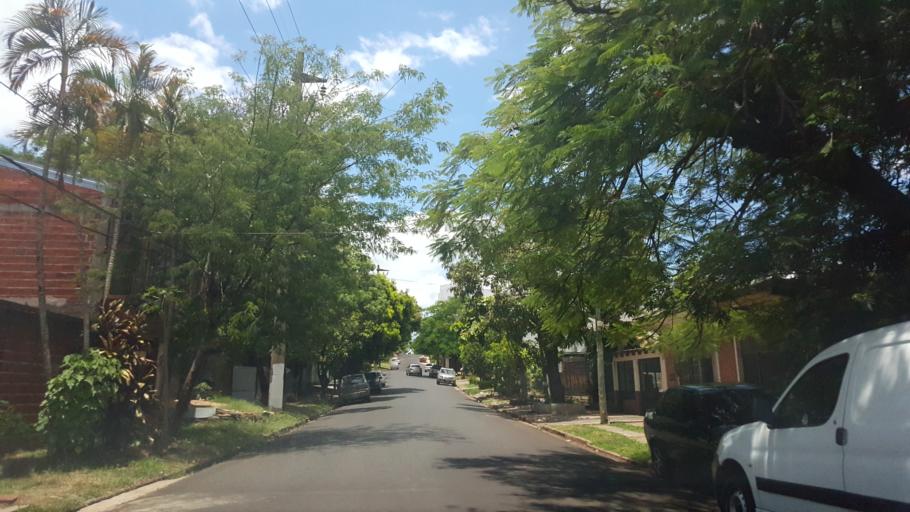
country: AR
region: Misiones
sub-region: Departamento de Capital
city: Posadas
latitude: -27.3583
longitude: -55.9014
